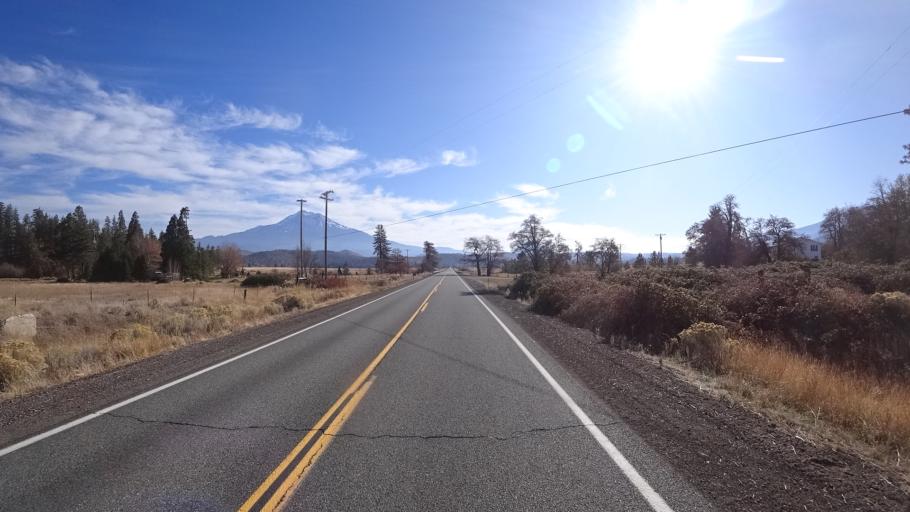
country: US
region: California
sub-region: Siskiyou County
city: Weed
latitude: 41.4487
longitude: -122.4514
